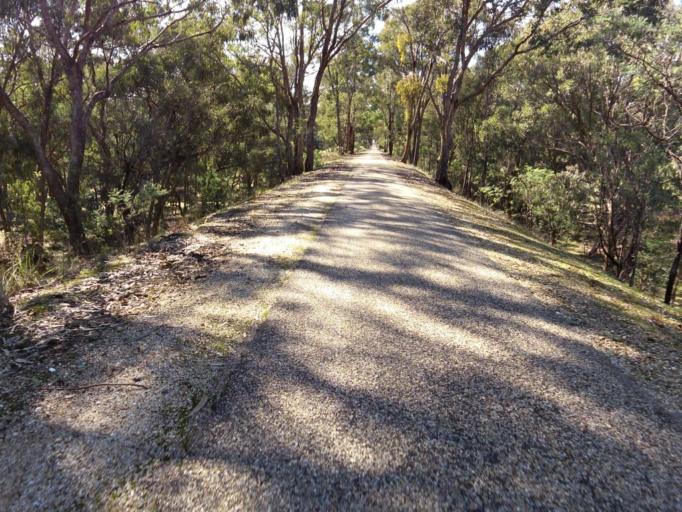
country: AU
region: Victoria
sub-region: Wangaratta
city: Wangaratta
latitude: -36.4057
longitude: 146.6227
